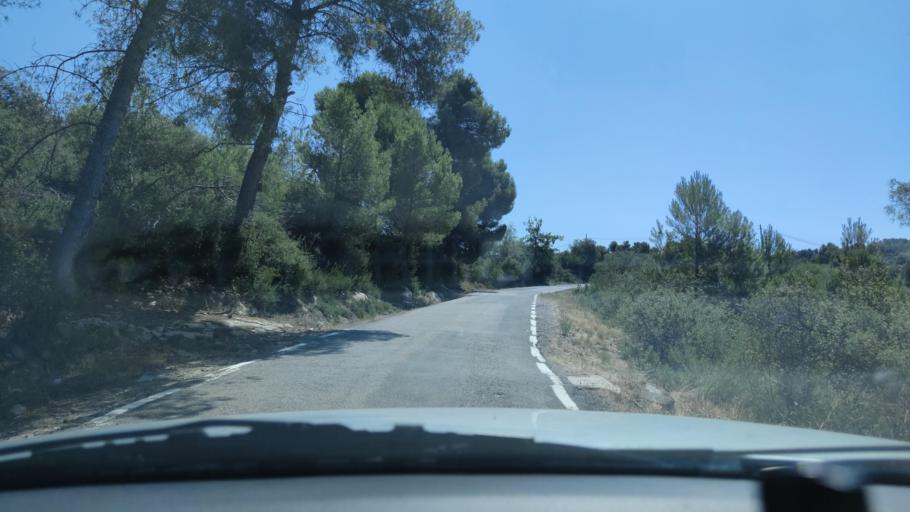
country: ES
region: Catalonia
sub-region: Provincia de Lleida
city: Fulleda
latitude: 41.4831
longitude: 1.0124
